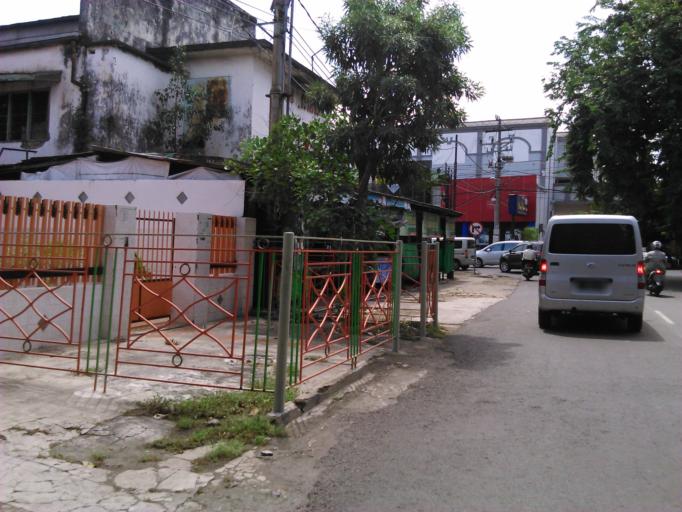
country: ID
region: East Java
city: Gubengairlangga
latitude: -7.2788
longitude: 112.7432
